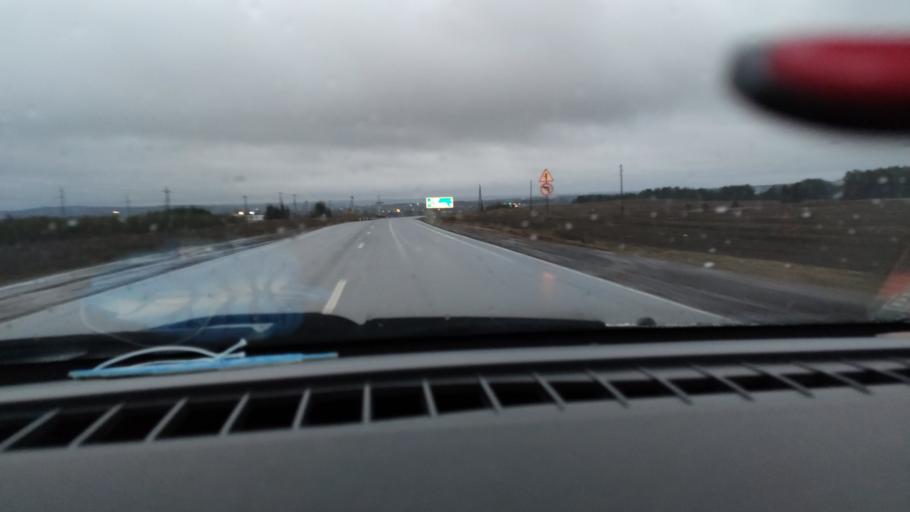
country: RU
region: Udmurtiya
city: Alnashi
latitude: 56.1954
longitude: 52.4551
